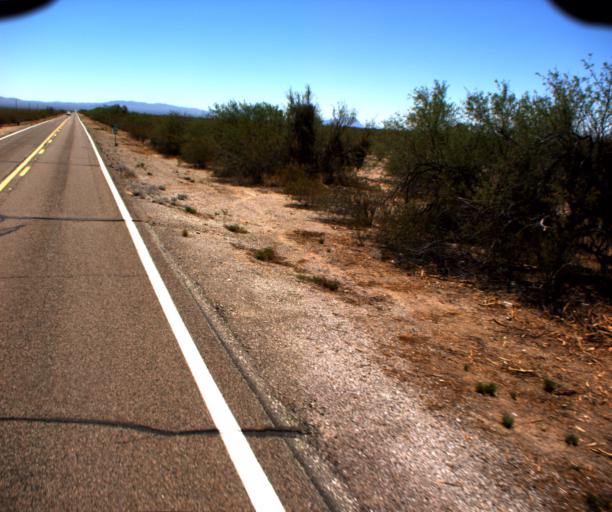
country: US
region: Arizona
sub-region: Pima County
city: Ajo
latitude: 32.2026
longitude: -112.5151
